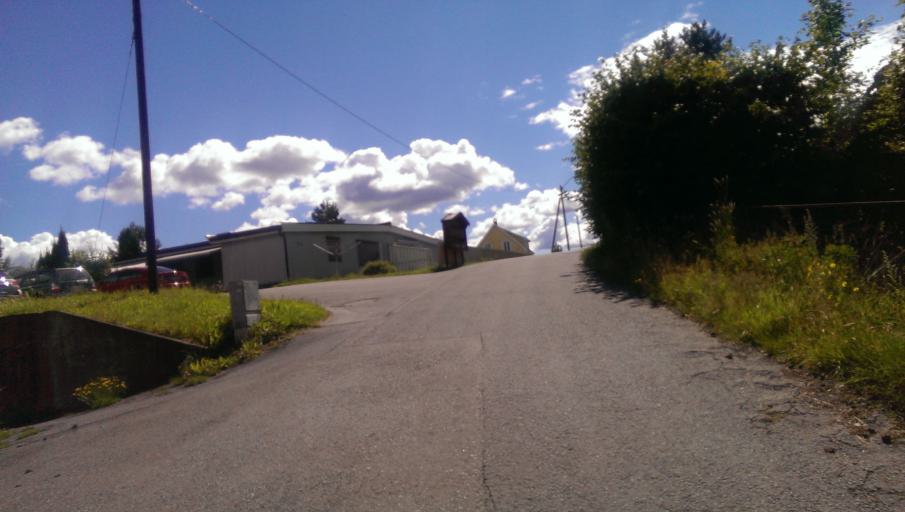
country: NO
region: Buskerud
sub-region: Kongsberg
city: Kongsberg
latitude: 59.6573
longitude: 9.6554
